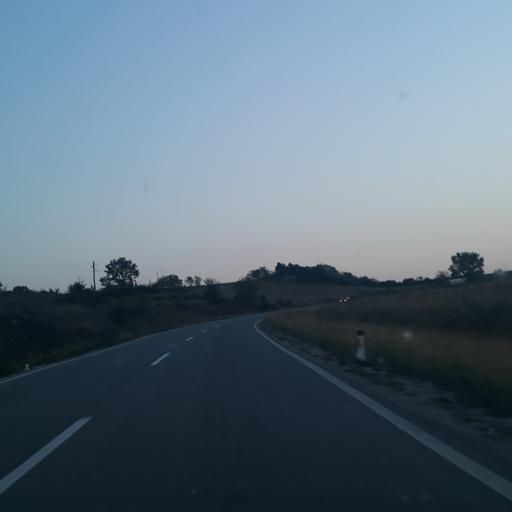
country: RS
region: Central Serbia
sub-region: Nisavski Okrug
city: Svrljig
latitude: 43.4383
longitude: 22.1637
